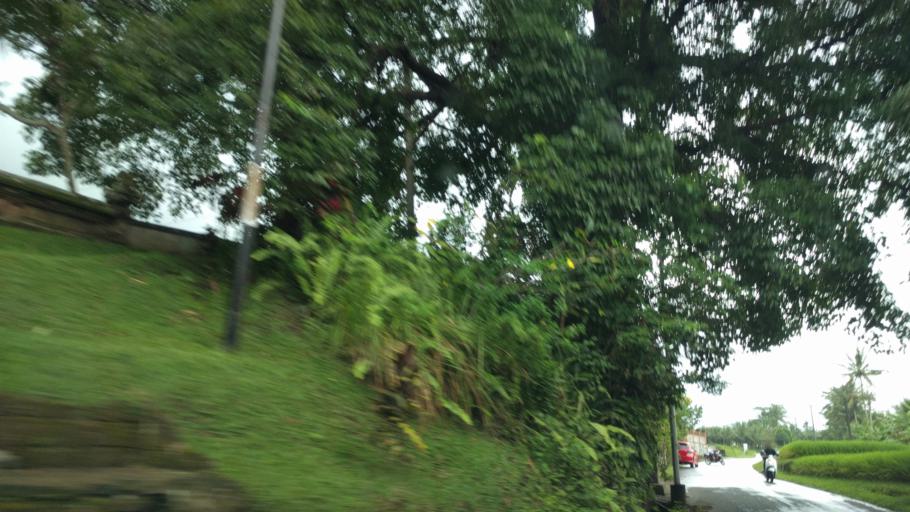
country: ID
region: Bali
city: Bunutan
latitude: -8.4701
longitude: 115.2600
